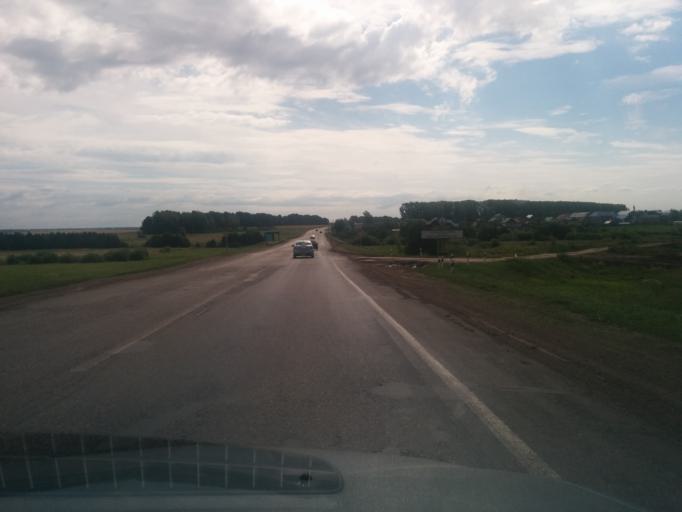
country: RU
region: Bashkortostan
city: Kabakovo
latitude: 54.4672
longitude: 55.9532
